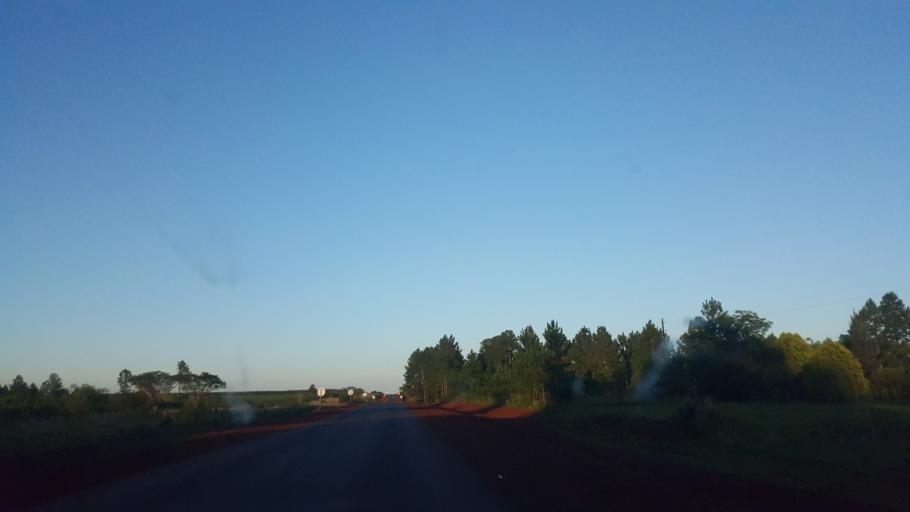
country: AR
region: Corrientes
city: Santo Tome
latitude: -28.5056
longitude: -56.0579
